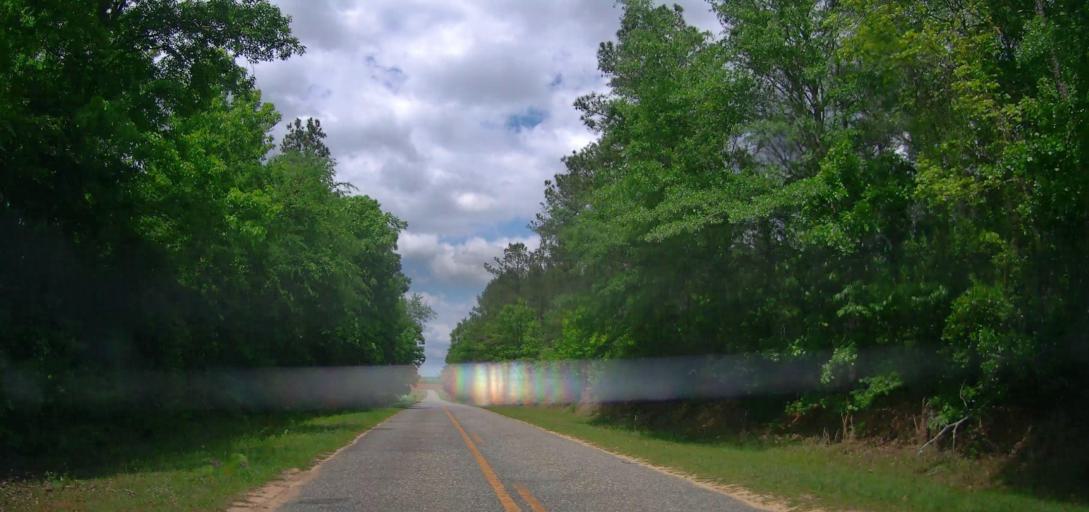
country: US
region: Georgia
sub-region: Laurens County
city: Dublin
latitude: 32.6060
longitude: -82.9383
